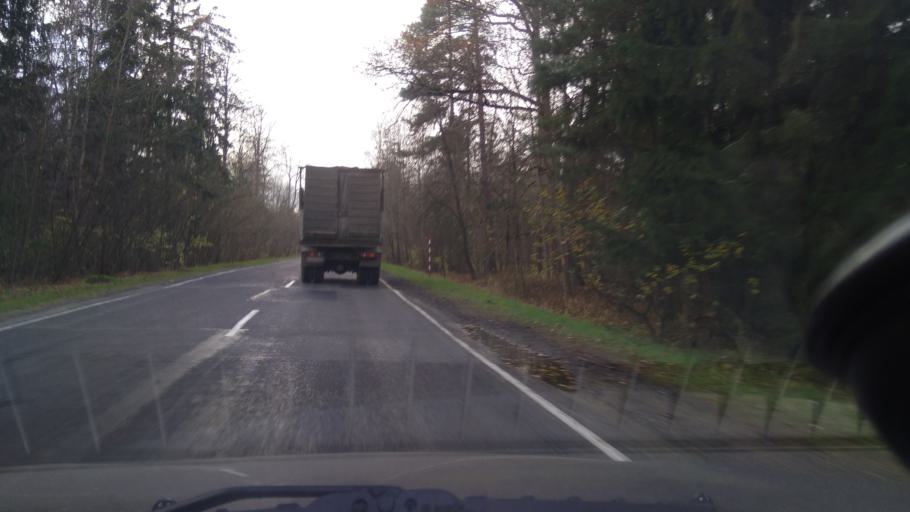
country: BY
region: Minsk
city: Slutsk
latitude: 53.2067
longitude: 27.7773
